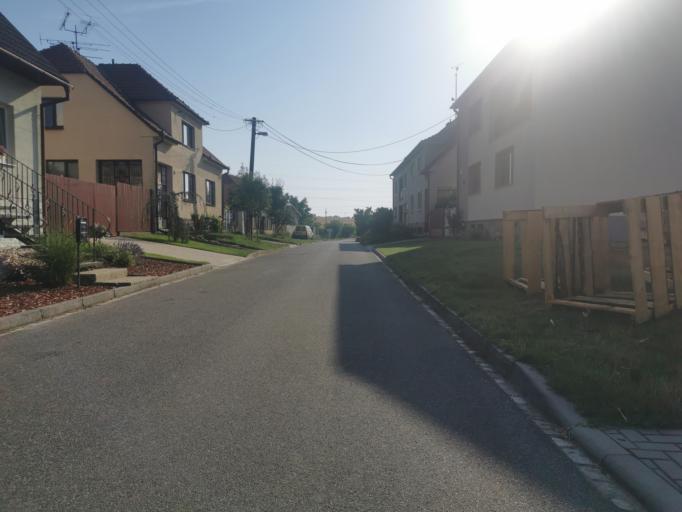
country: CZ
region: South Moravian
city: Vacenovice
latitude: 48.9439
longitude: 17.1710
